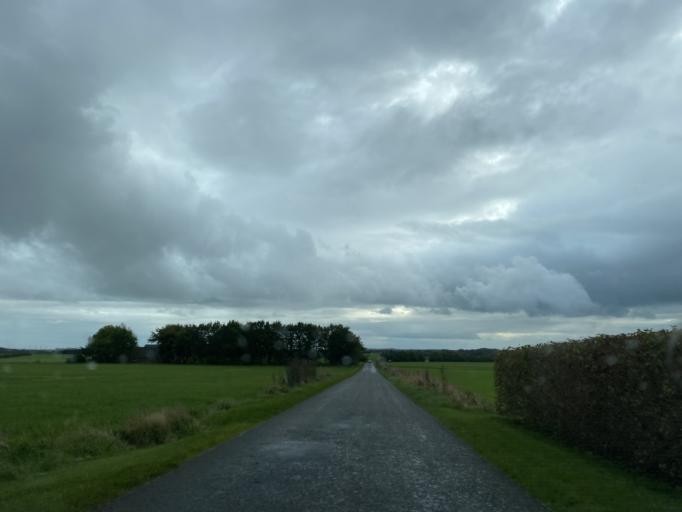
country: DK
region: Central Jutland
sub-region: Viborg Kommune
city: Bjerringbro
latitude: 56.3319
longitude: 9.7092
